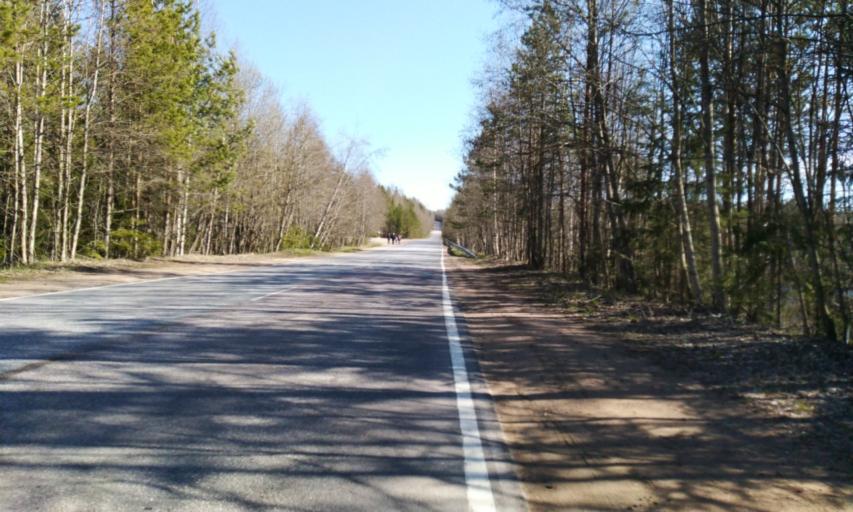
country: RU
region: Leningrad
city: Garbolovo
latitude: 60.3796
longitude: 30.4629
